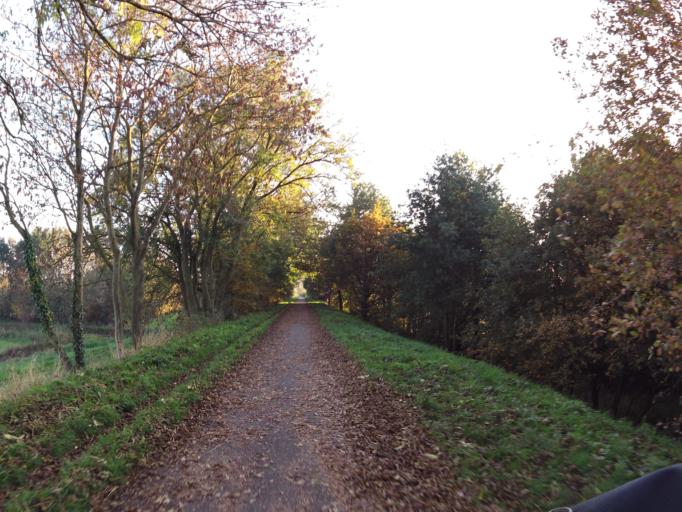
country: NL
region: Gelderland
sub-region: Gemeente Zaltbommel
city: Nederhemert-Noord
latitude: 51.7163
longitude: 5.1904
